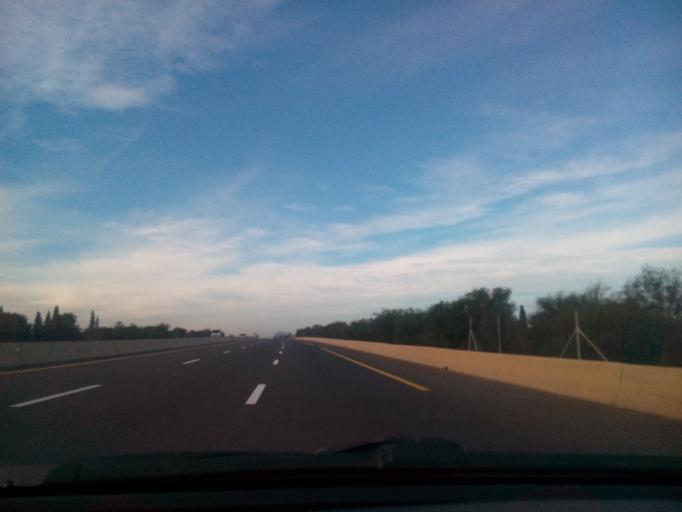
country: DZ
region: Mascara
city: Mascara
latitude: 35.6214
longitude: 0.0487
